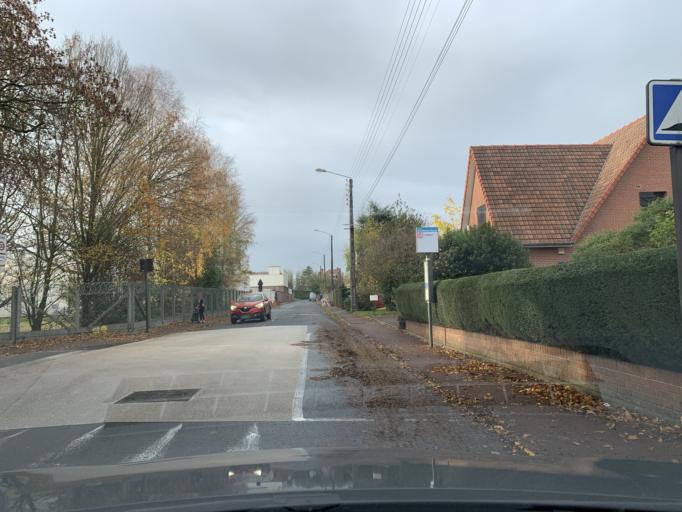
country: FR
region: Nord-Pas-de-Calais
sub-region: Departement du Nord
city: Douai
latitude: 50.3584
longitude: 3.0843
